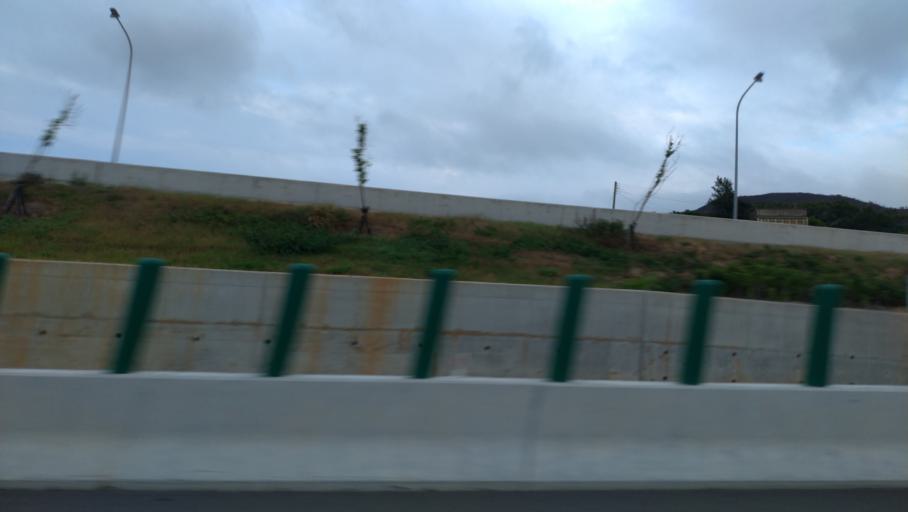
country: TW
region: Taiwan
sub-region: Miaoli
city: Miaoli
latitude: 24.5419
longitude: 120.7011
